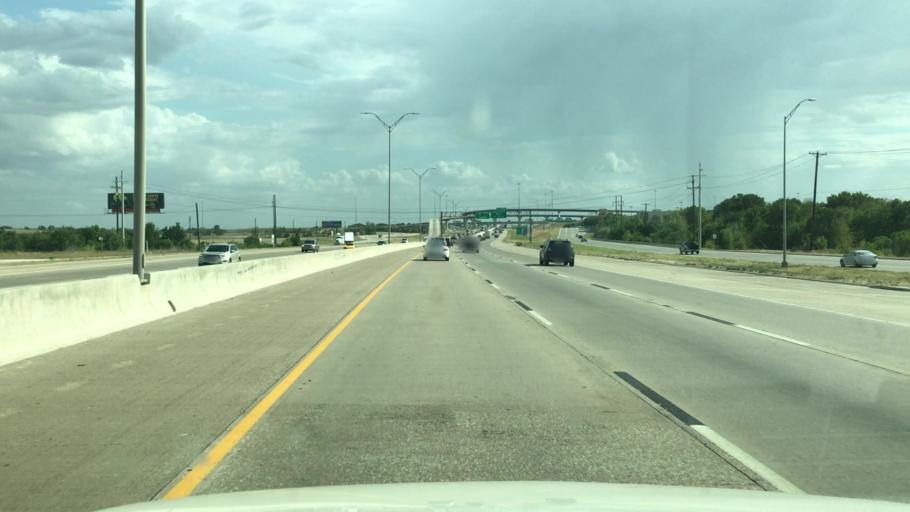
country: US
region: Texas
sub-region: McLennan County
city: Beverly Hills
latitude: 31.5037
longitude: -97.1452
